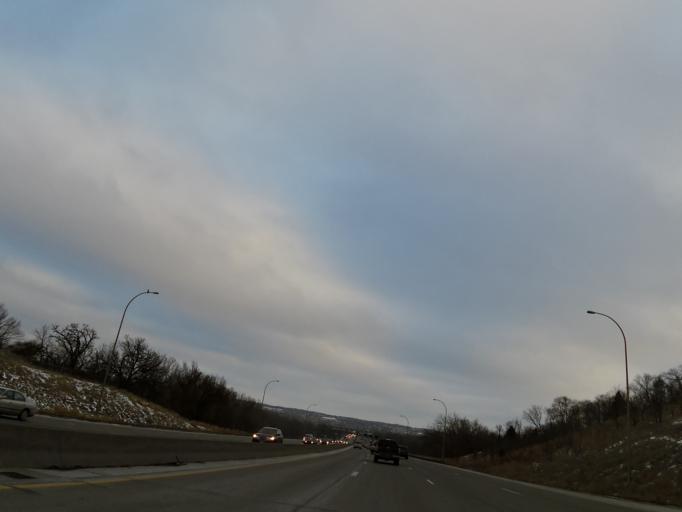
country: US
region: Minnesota
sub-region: Hennepin County
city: Bloomington
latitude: 44.8078
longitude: -93.2915
